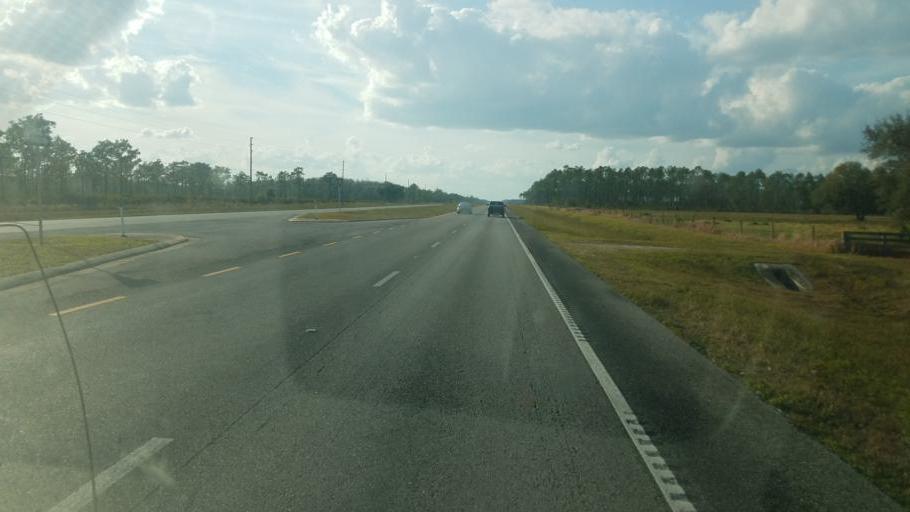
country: US
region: Florida
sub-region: Osceola County
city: Saint Cloud
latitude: 28.1359
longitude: -81.0300
